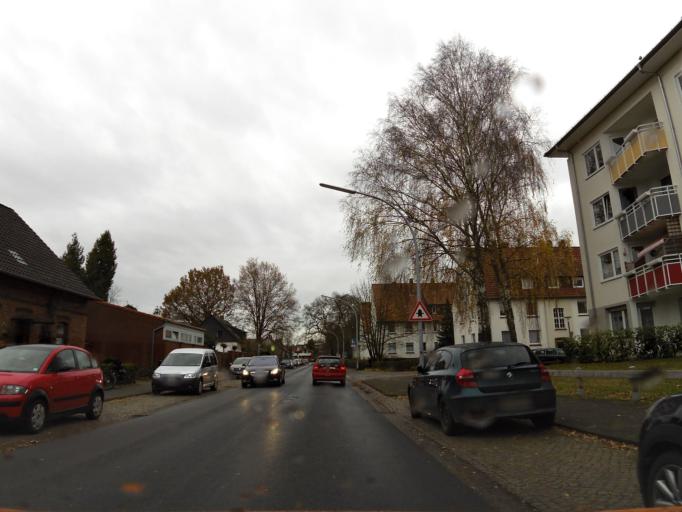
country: DE
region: Lower Saxony
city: Oldenburg
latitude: 53.1176
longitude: 8.2180
